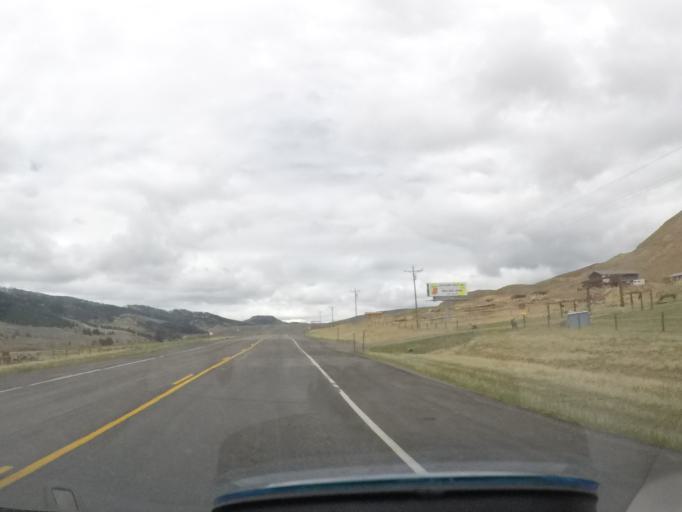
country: US
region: Wyoming
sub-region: Sublette County
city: Pinedale
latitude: 43.5716
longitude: -109.7211
